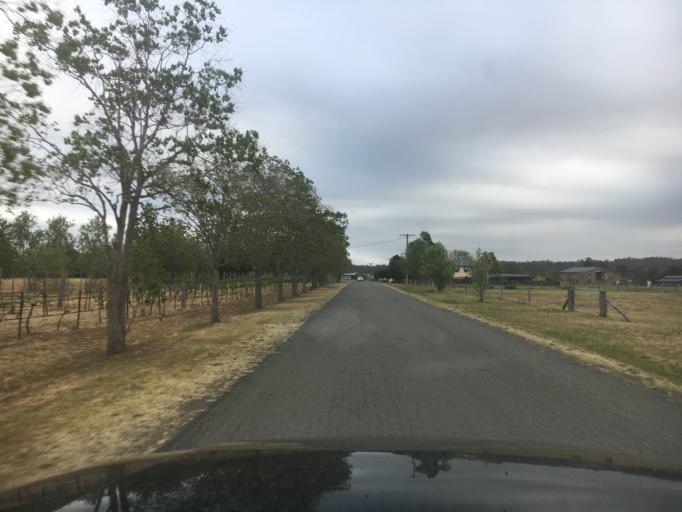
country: AU
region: New South Wales
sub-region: Singleton
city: Singleton
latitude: -32.5636
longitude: 151.1891
